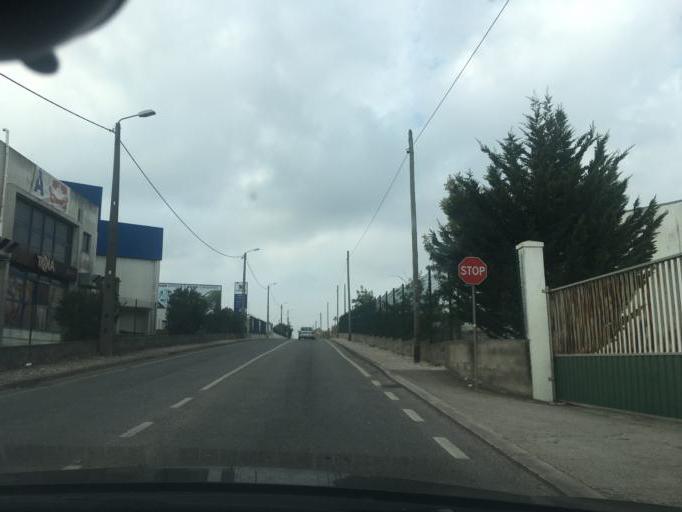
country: PT
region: Lisbon
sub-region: Sintra
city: Sintra
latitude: 38.8351
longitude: -9.3574
